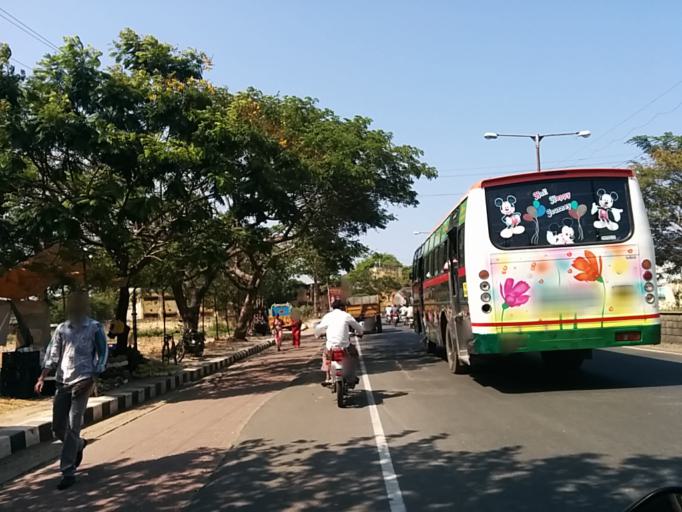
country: IN
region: Pondicherry
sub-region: Puducherry
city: Puducherry
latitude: 11.9427
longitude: 79.8083
